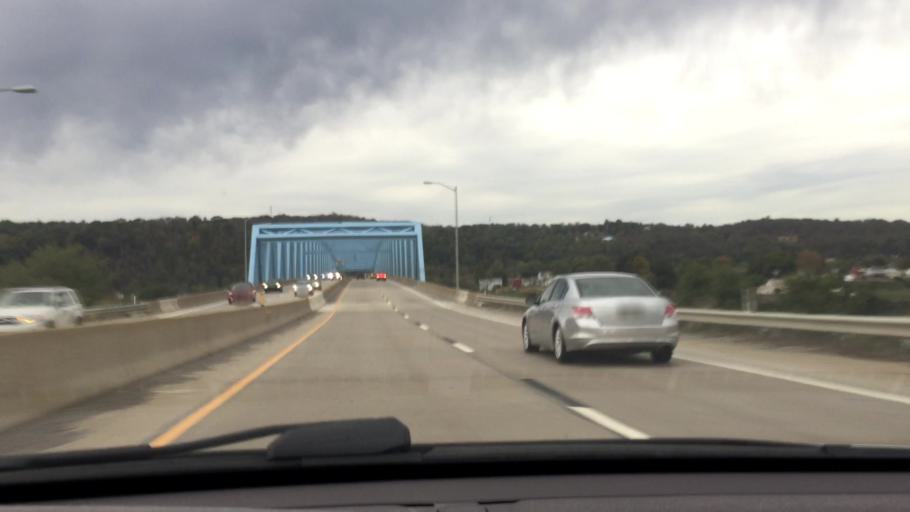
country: US
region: Pennsylvania
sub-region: Beaver County
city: Beaver
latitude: 40.6764
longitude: -80.3298
